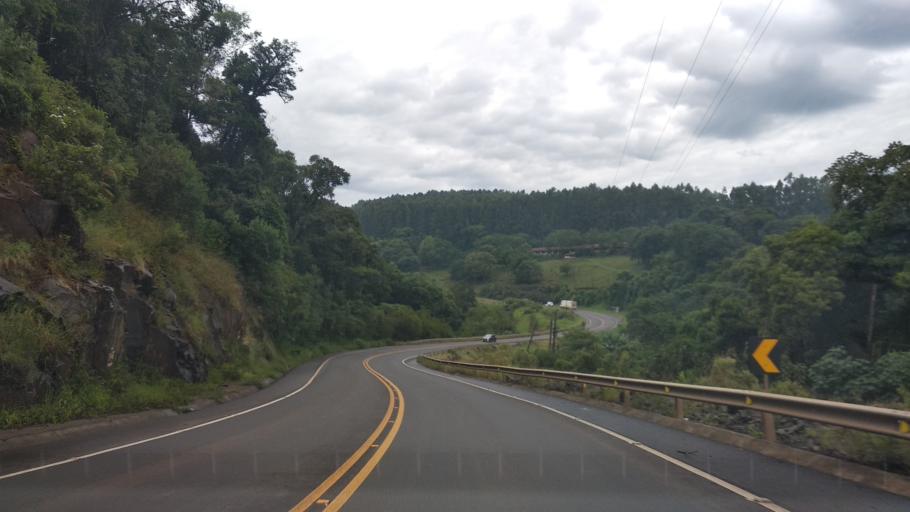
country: BR
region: Santa Catarina
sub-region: Videira
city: Videira
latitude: -27.0634
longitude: -51.2370
